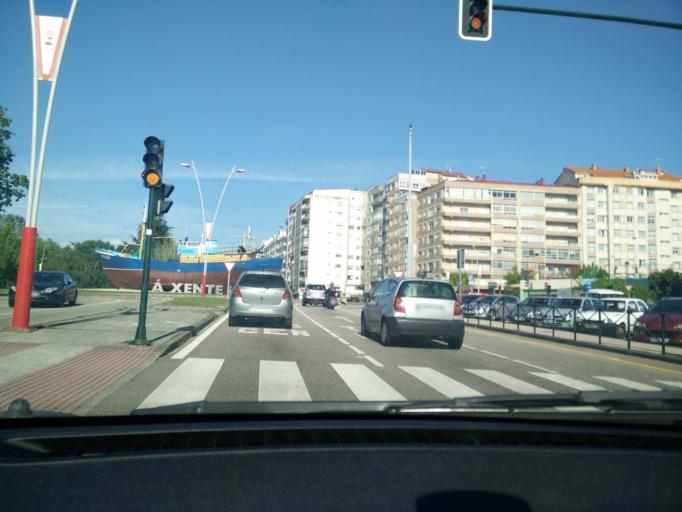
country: ES
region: Galicia
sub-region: Provincia de Pontevedra
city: Vigo
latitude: 42.2181
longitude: -8.7451
